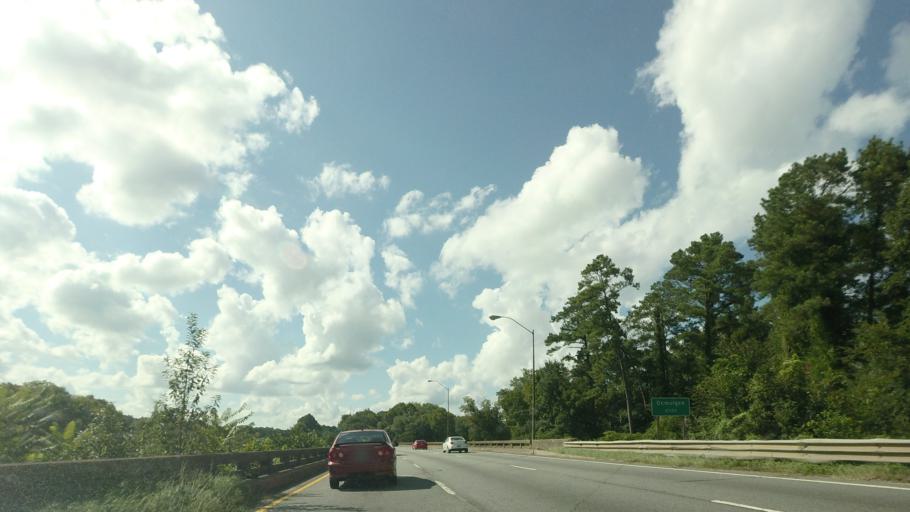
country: US
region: Georgia
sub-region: Bibb County
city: Macon
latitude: 32.8538
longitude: -83.6337
